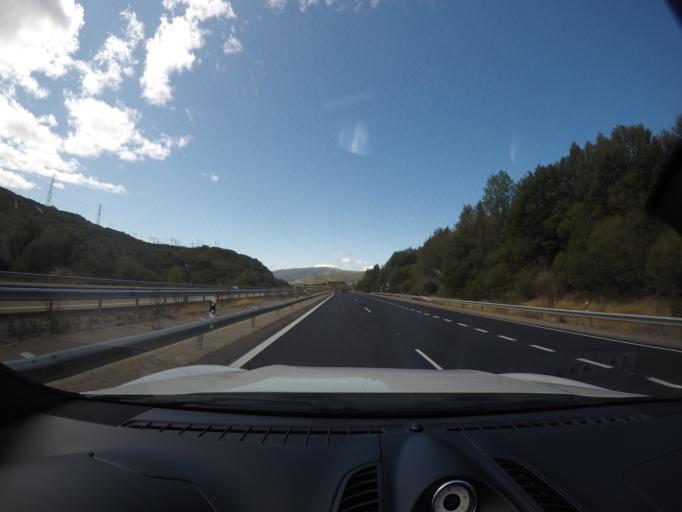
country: ES
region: Castille and Leon
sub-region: Provincia de Zamora
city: Lubian
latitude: 42.0351
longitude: -6.8544
